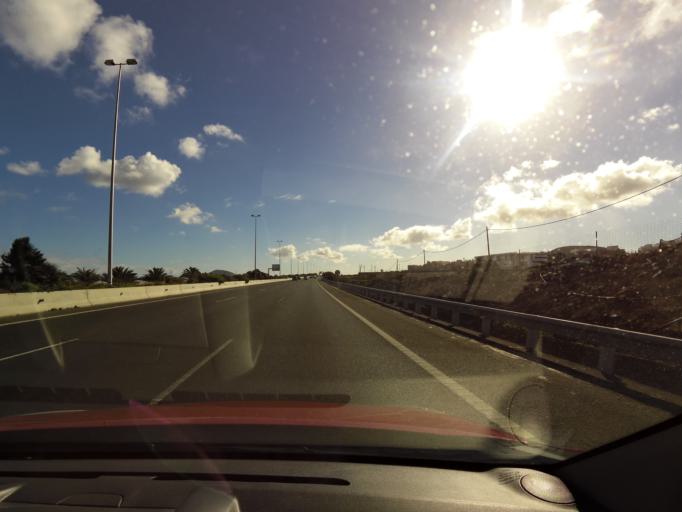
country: ES
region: Canary Islands
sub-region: Provincia de Las Palmas
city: Ingenio
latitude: 27.9142
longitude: -15.3987
